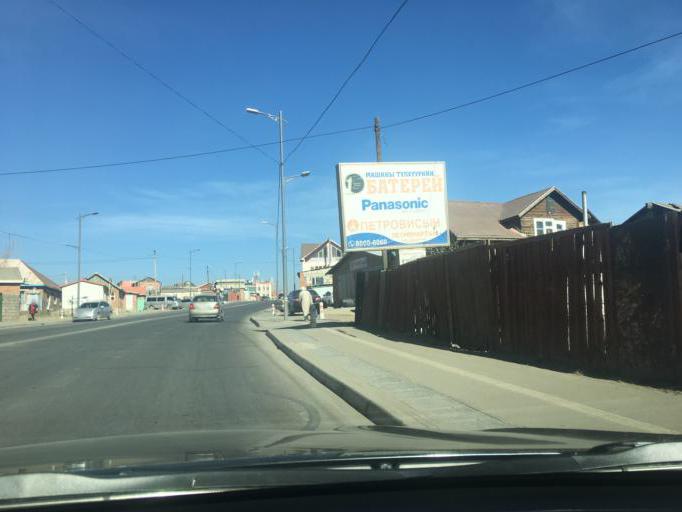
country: MN
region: Ulaanbaatar
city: Ulaanbaatar
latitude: 47.9160
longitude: 106.7805
